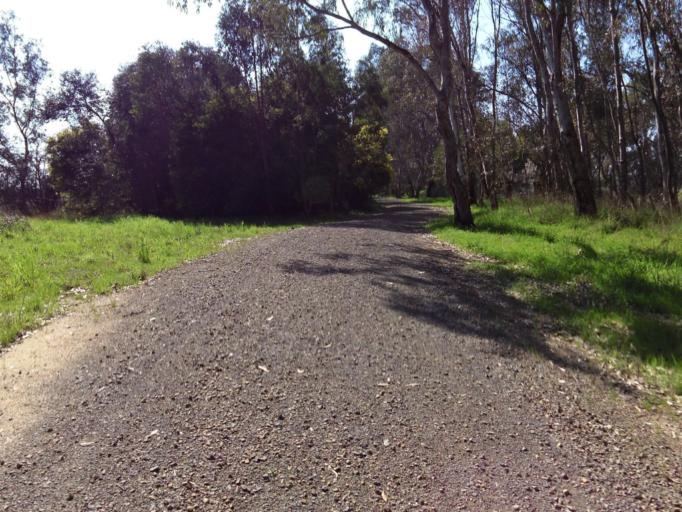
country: AU
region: Victoria
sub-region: Murrindindi
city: Alexandra
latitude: -37.1507
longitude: 145.5820
